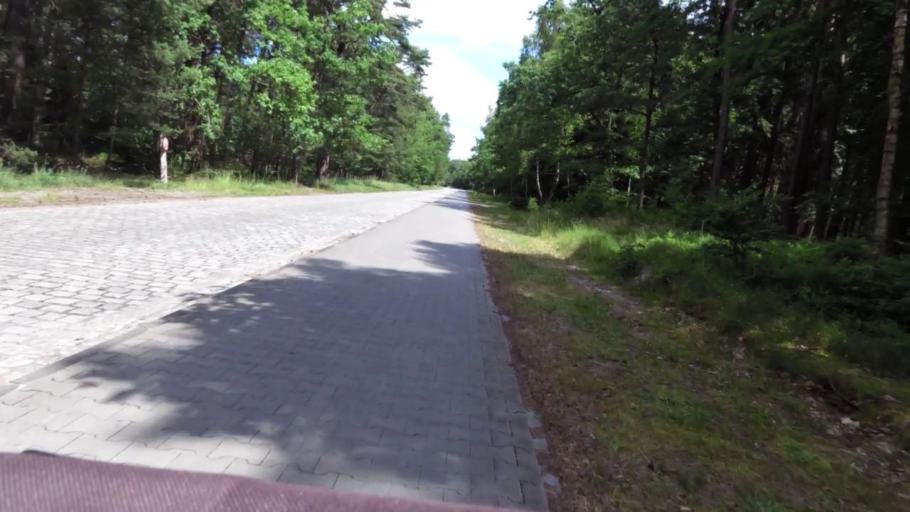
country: PL
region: West Pomeranian Voivodeship
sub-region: Powiat gryficki
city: Mrzezyno
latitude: 54.1352
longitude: 15.2711
